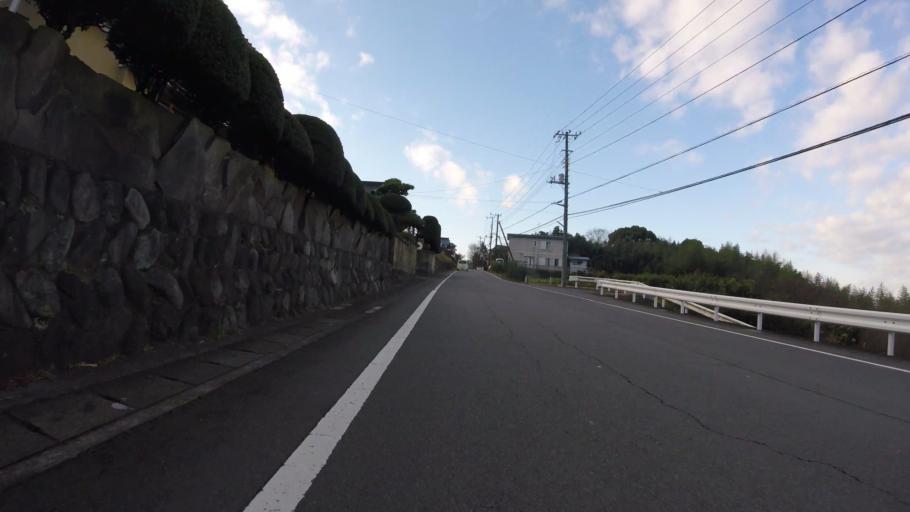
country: JP
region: Shizuoka
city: Mishima
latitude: 35.0975
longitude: 138.9629
